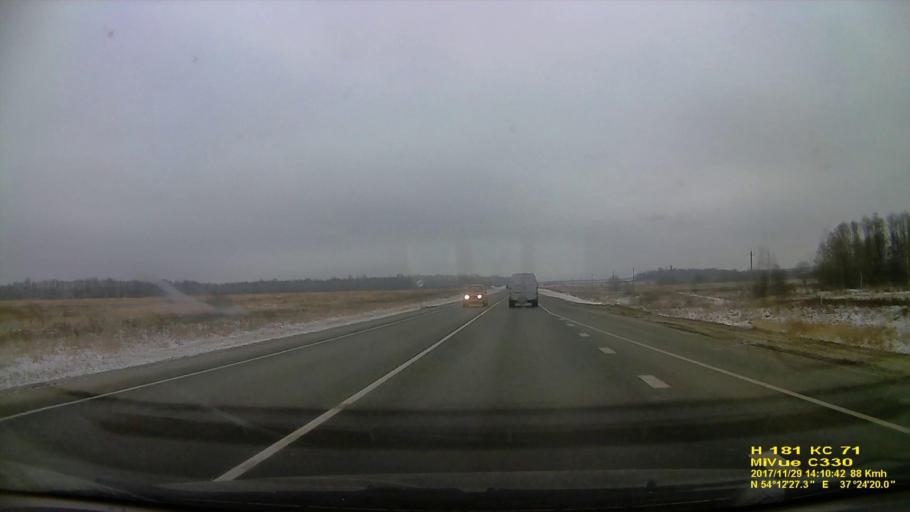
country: RU
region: Tula
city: Leninskiy
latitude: 54.2072
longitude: 37.4061
